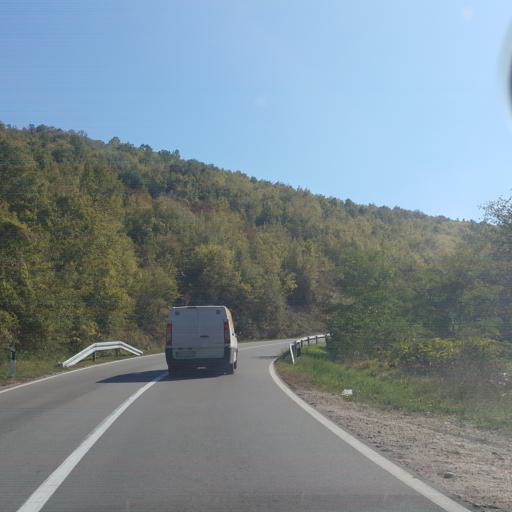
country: RS
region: Central Serbia
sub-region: Zajecarski Okrug
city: Knjazevac
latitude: 43.5338
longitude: 22.2255
